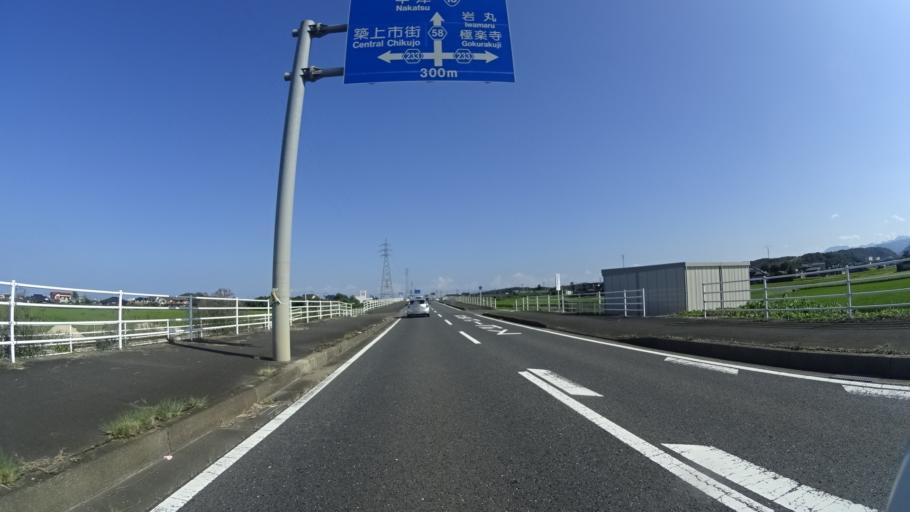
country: JP
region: Fukuoka
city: Shiida
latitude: 33.6531
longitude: 131.0480
